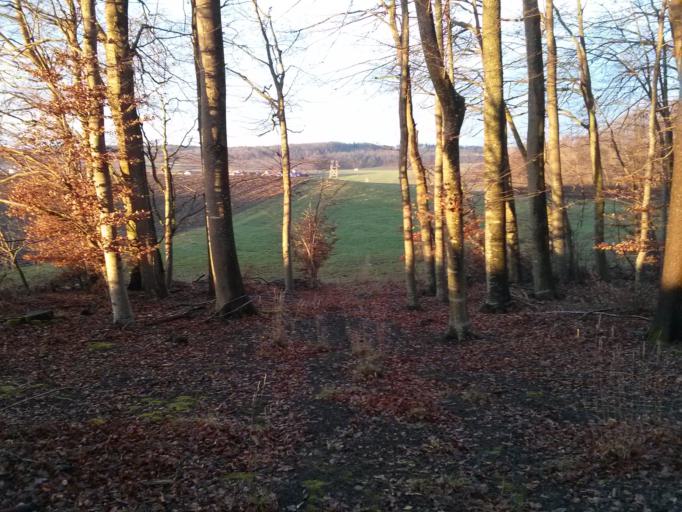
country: DE
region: Bavaria
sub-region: Swabia
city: Harburg
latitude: 48.7502
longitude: 10.6761
